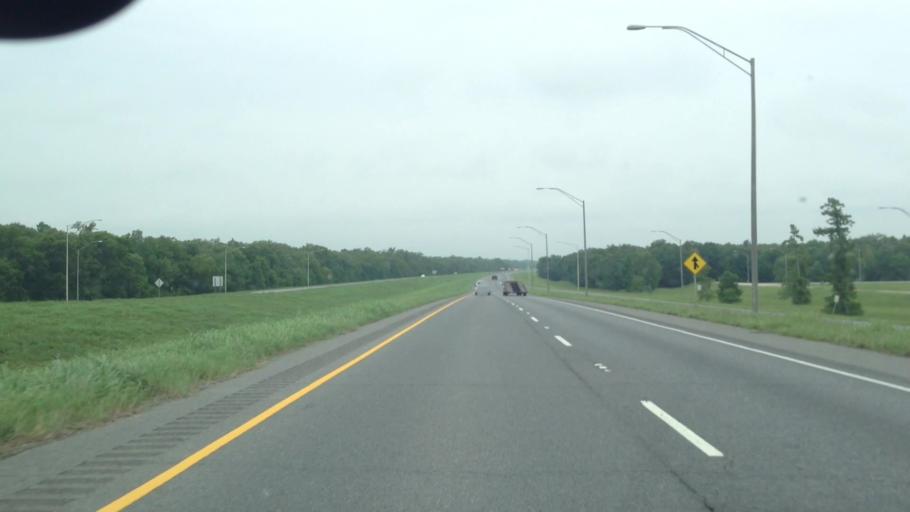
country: US
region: Louisiana
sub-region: Evangeline Parish
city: Ville Platte
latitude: 30.7258
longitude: -92.1206
